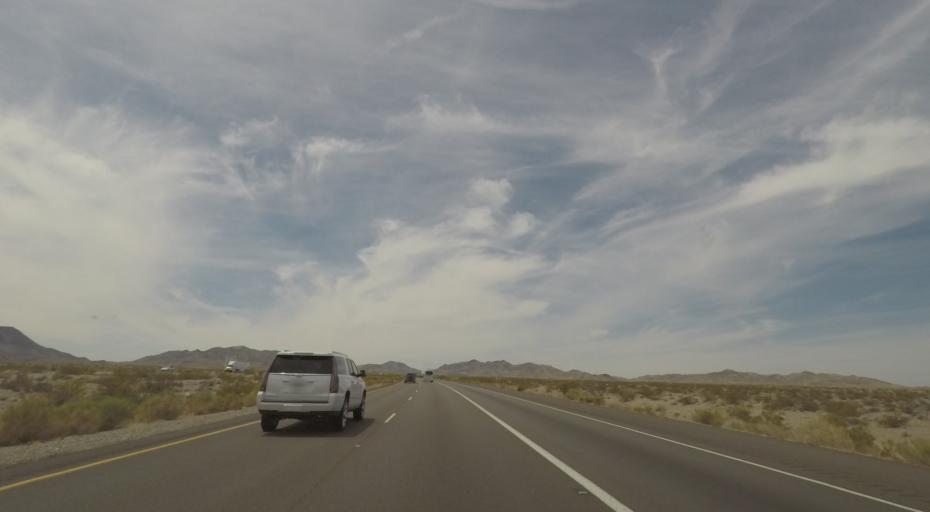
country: US
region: California
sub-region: San Bernardino County
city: Needles
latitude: 34.8823
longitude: -114.7896
